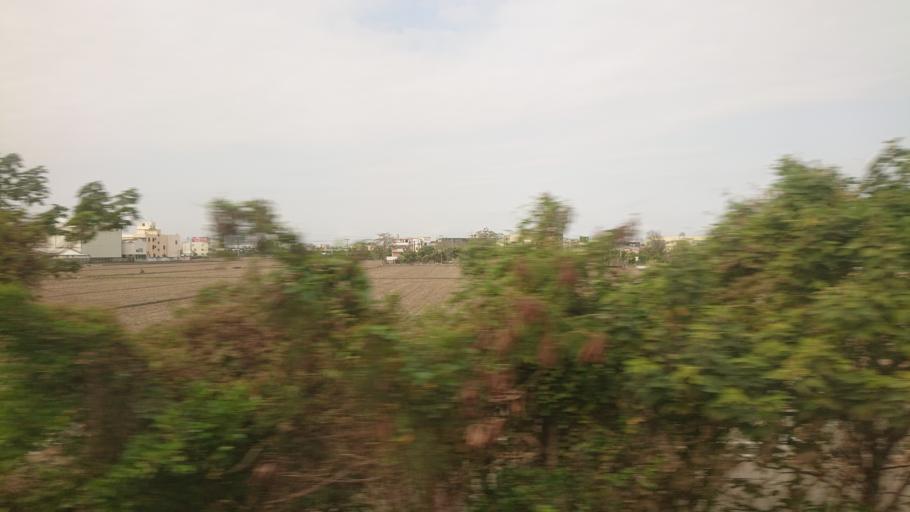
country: TW
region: Taiwan
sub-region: Changhua
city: Chang-hua
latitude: 24.0534
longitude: 120.5297
